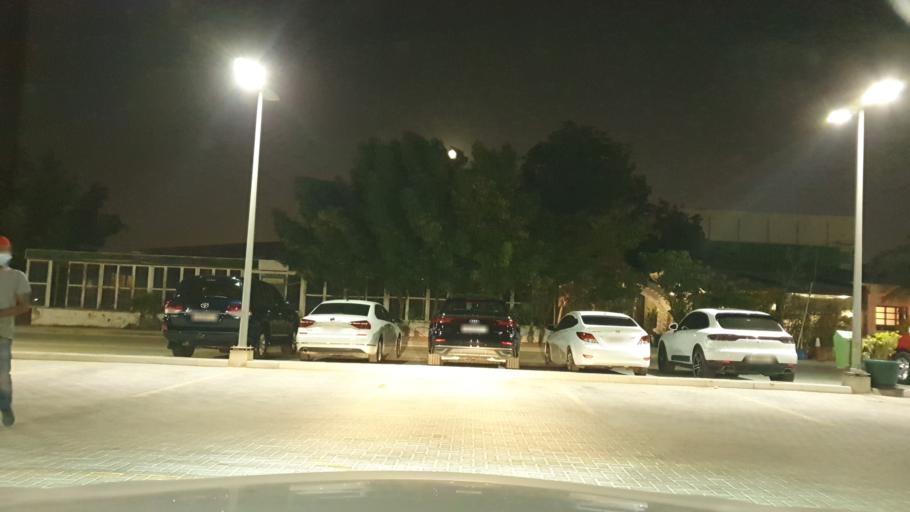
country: BH
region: Manama
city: Jidd Hafs
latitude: 26.1981
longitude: 50.4764
